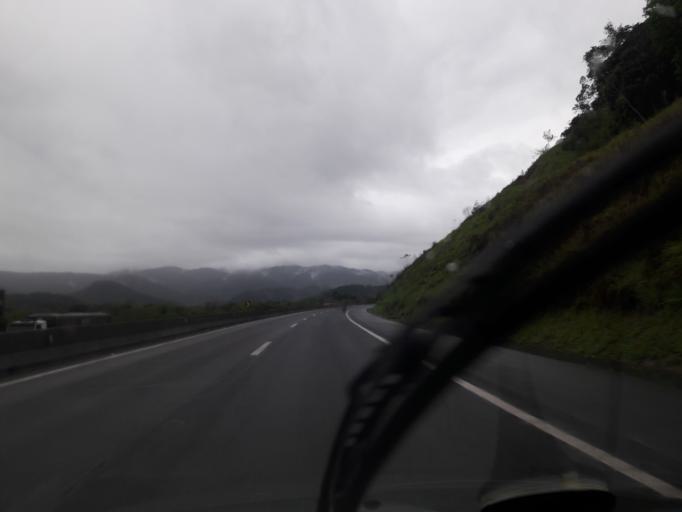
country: BR
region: Sao Paulo
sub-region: Miracatu
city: Miracatu
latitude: -24.2092
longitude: -47.3714
